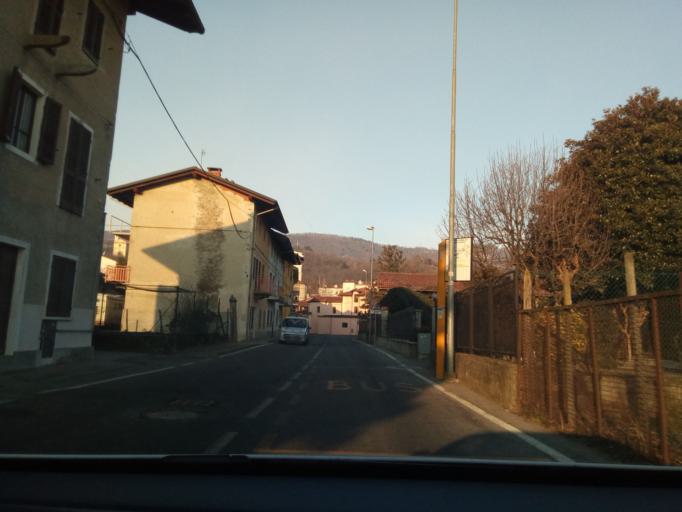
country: IT
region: Piedmont
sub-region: Provincia di Torino
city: Fiorano Canavese
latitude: 45.4685
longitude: 7.8336
